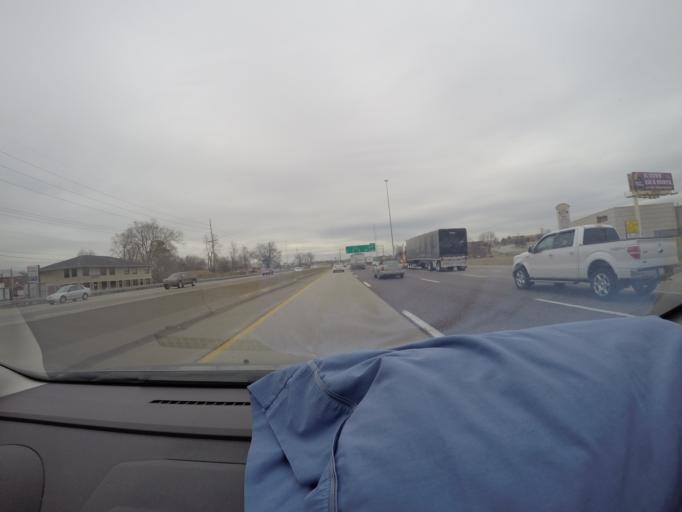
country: US
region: Missouri
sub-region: Saint Charles County
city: Saint Peters
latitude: 38.8002
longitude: -90.6267
